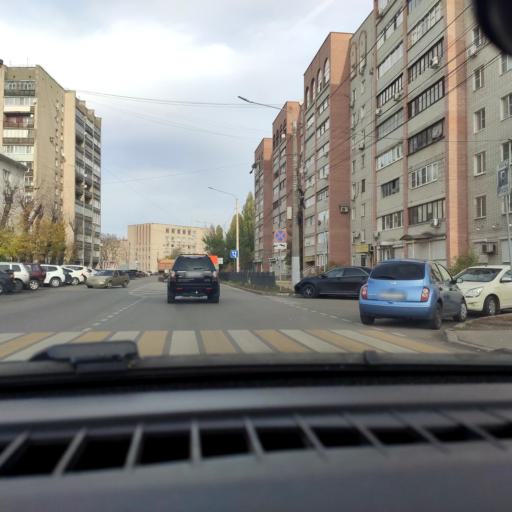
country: RU
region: Voronezj
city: Voronezh
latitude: 51.6520
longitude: 39.1866
